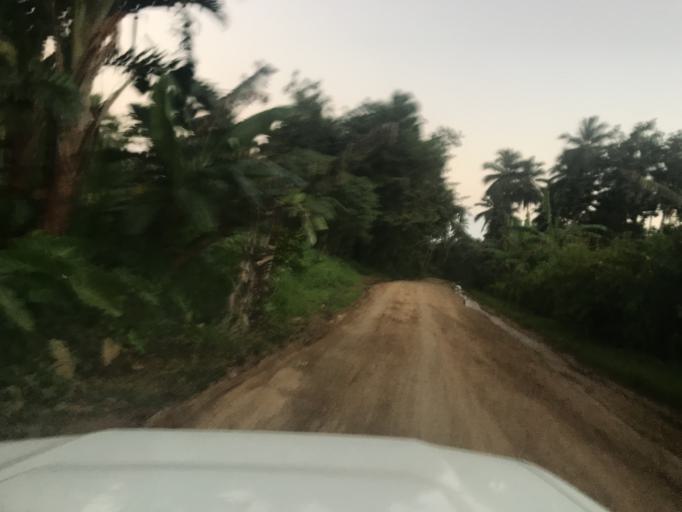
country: VU
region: Sanma
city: Luganville
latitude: -15.5552
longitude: 166.9941
